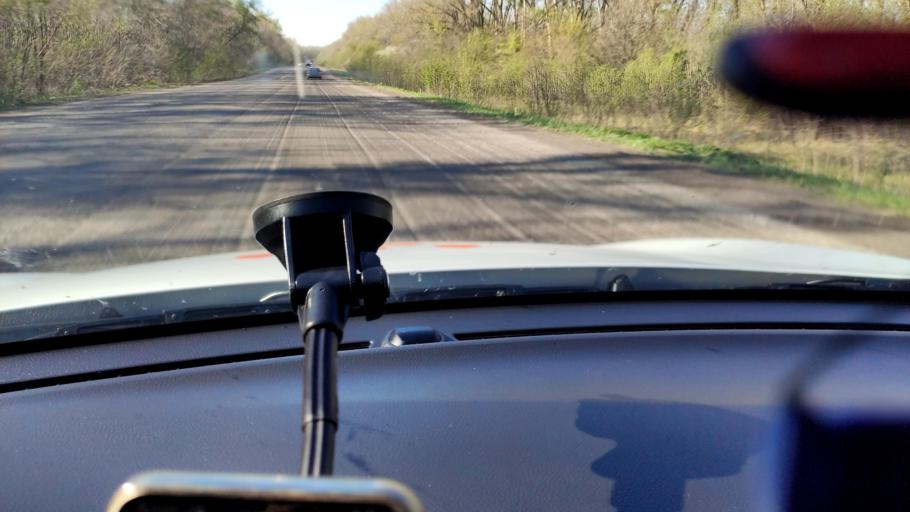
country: RU
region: Voronezj
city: Uryv-Pokrovka
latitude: 51.2176
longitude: 39.0679
